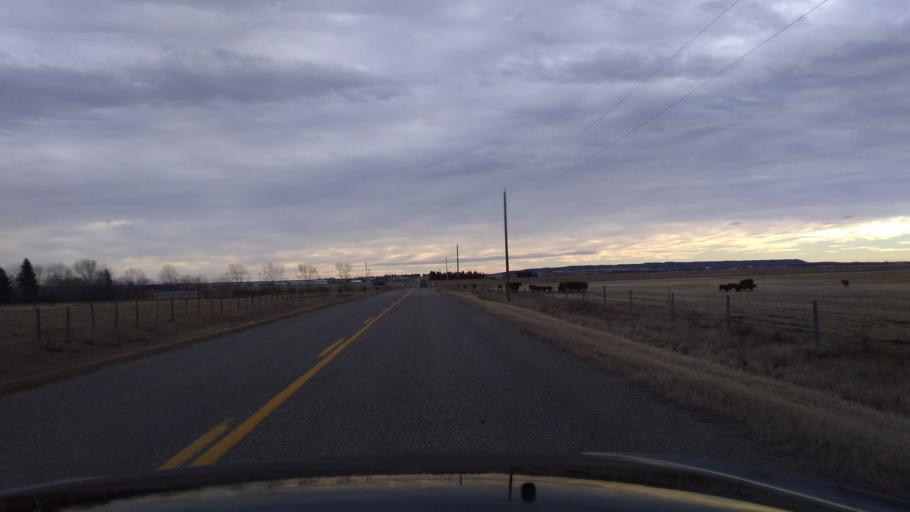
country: CA
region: Alberta
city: Cochrane
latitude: 51.0960
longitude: -114.4015
